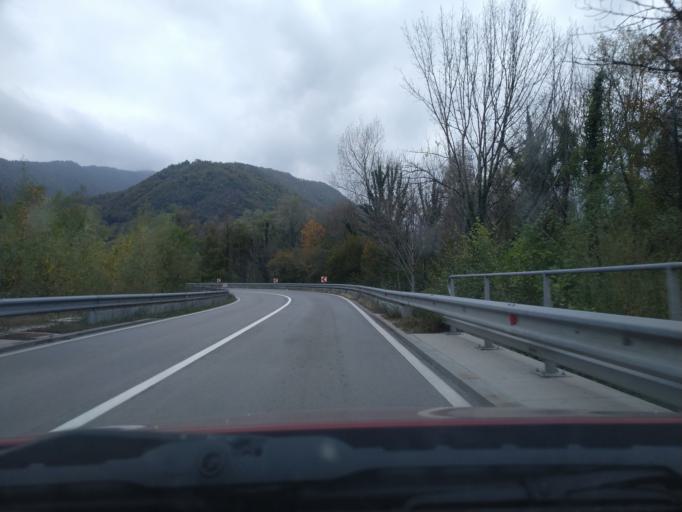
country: SI
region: Tolmin
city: Tolmin
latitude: 46.1835
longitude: 13.7184
